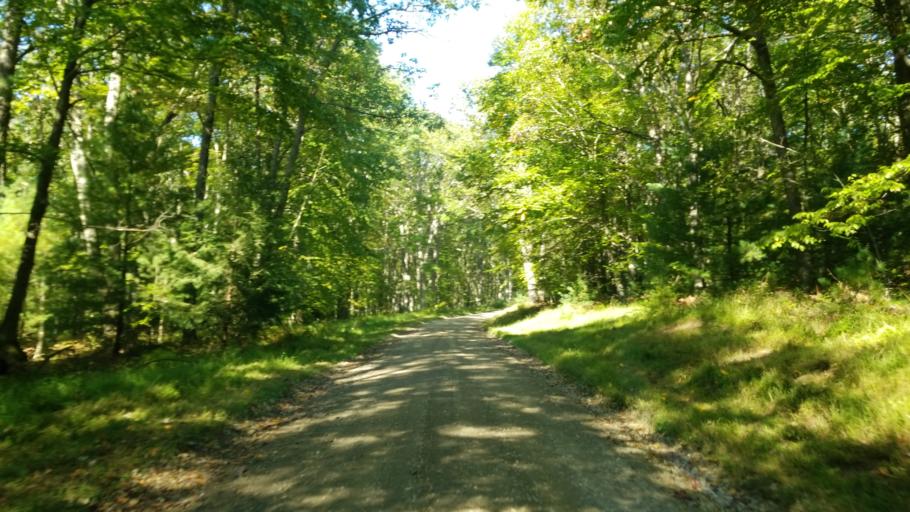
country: US
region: Pennsylvania
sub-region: Clearfield County
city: Curwensville
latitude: 41.1136
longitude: -78.5698
